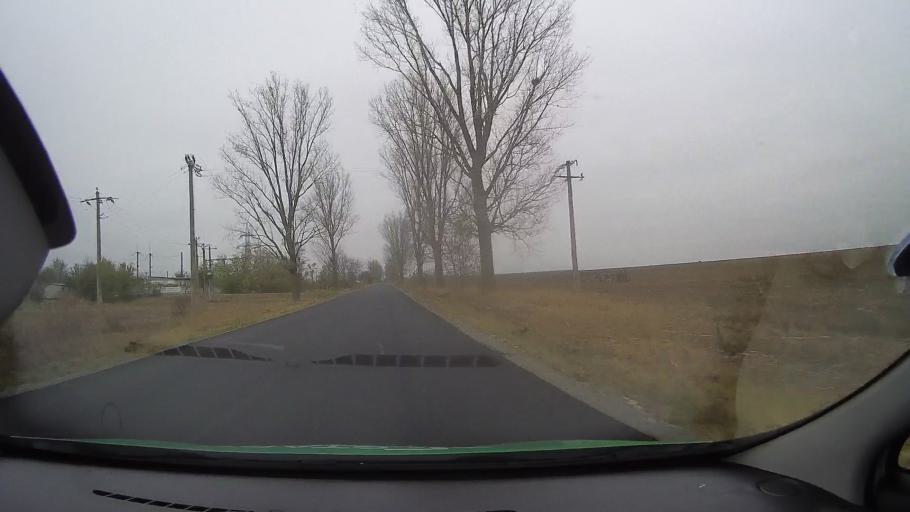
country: RO
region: Ialomita
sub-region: Comuna Valea Ciorii
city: Valea Ciorii
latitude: 44.7505
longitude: 27.5687
